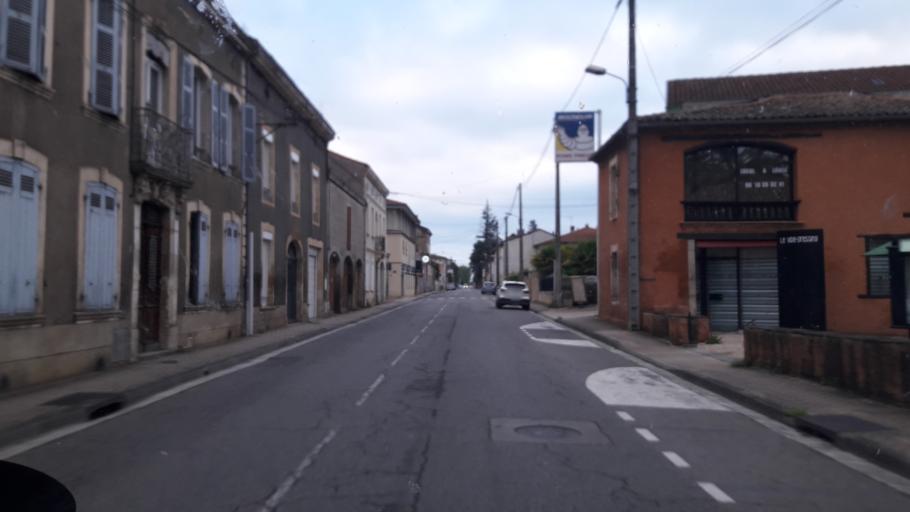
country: FR
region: Midi-Pyrenees
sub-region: Departement de la Haute-Garonne
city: Cazeres
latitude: 43.2087
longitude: 1.0857
